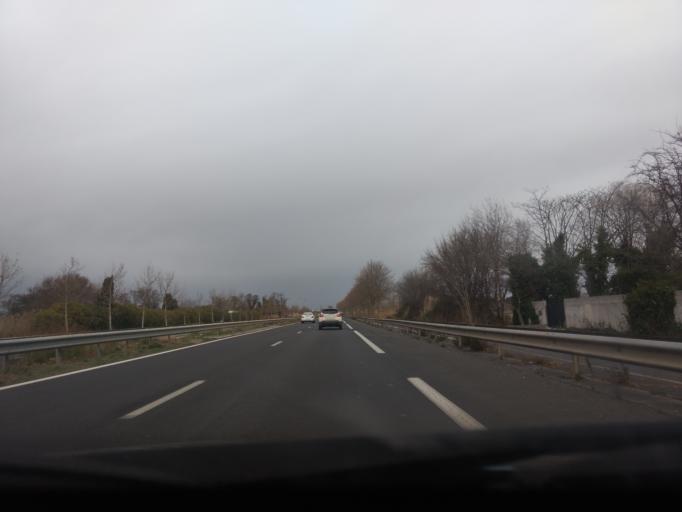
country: FR
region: Languedoc-Roussillon
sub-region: Departement de l'Herault
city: Lattes
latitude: 43.5634
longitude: 3.8943
